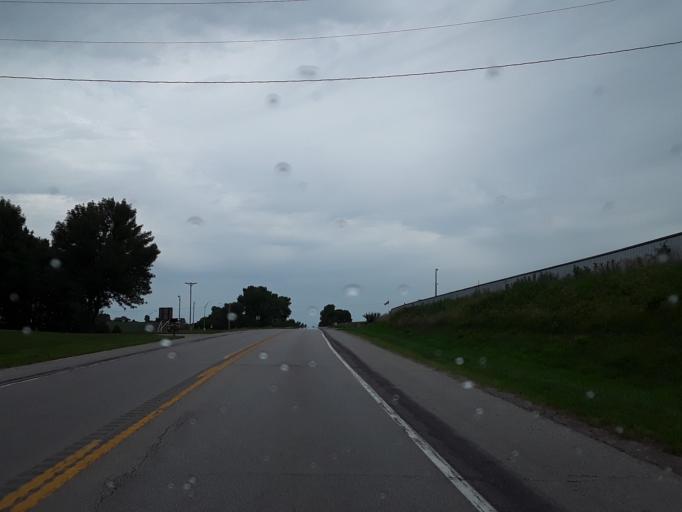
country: US
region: Nebraska
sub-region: Washington County
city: Blair
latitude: 41.5067
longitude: -96.1573
